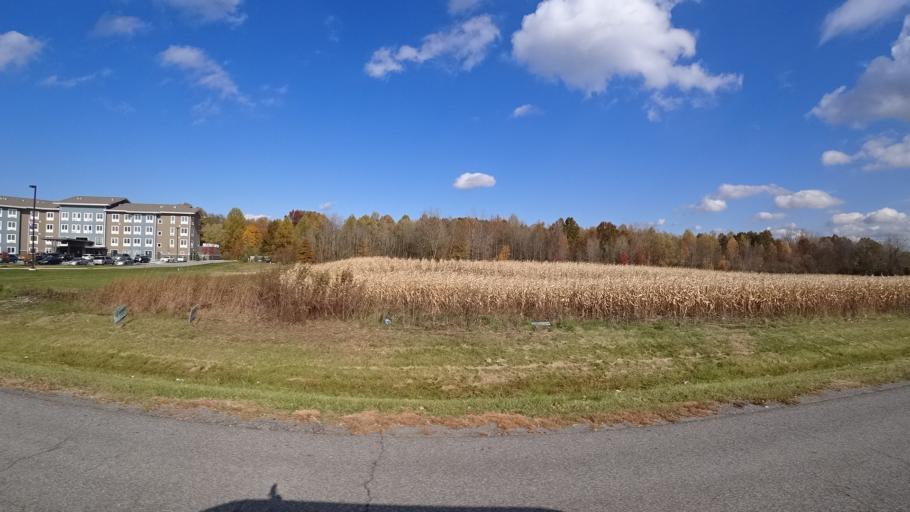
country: US
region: Indiana
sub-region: LaPorte County
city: Trail Creek
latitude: 41.6998
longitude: -86.8335
